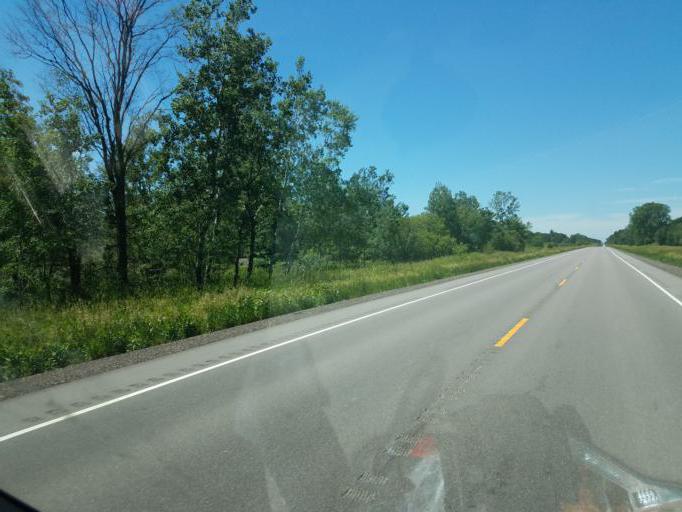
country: US
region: Wisconsin
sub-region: Juneau County
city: New Lisbon
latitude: 44.0251
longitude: -90.1661
